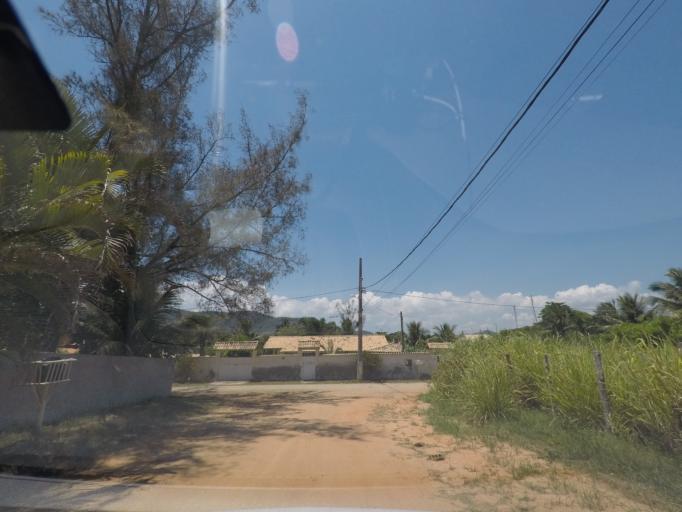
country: BR
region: Rio de Janeiro
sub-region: Niteroi
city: Niteroi
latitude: -22.9684
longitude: -42.9846
